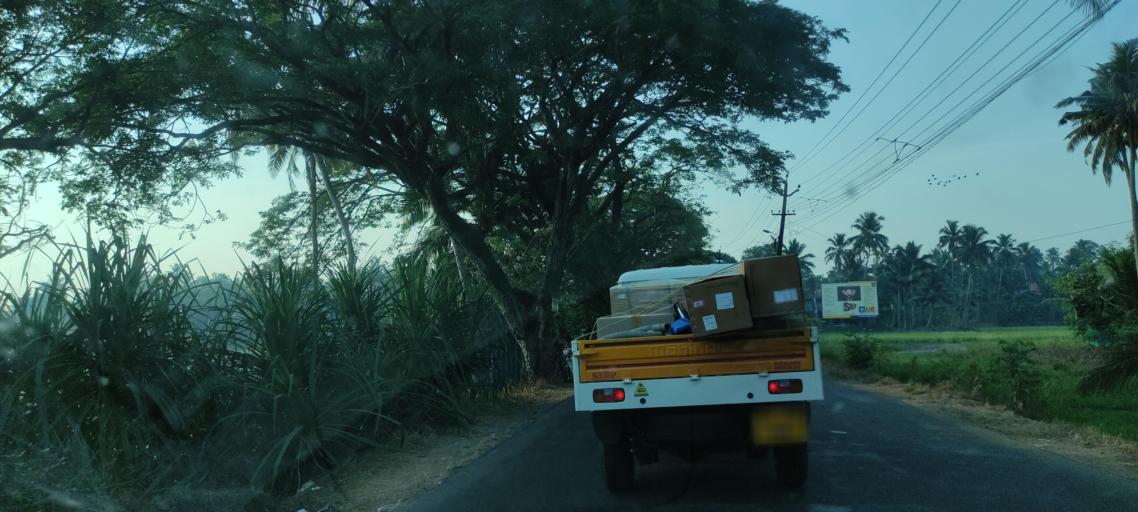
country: IN
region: Kerala
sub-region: Alappuzha
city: Shertallai
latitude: 9.6520
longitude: 76.4293
